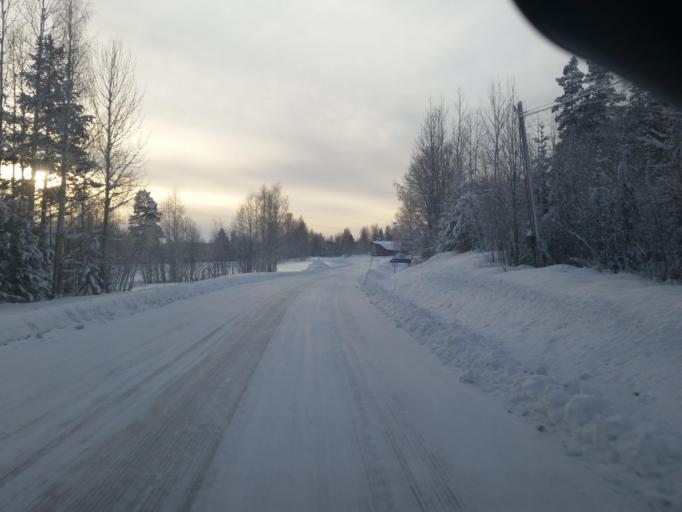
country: SE
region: Norrbotten
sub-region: Pitea Kommun
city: Norrfjarden
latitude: 65.5321
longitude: 21.4893
